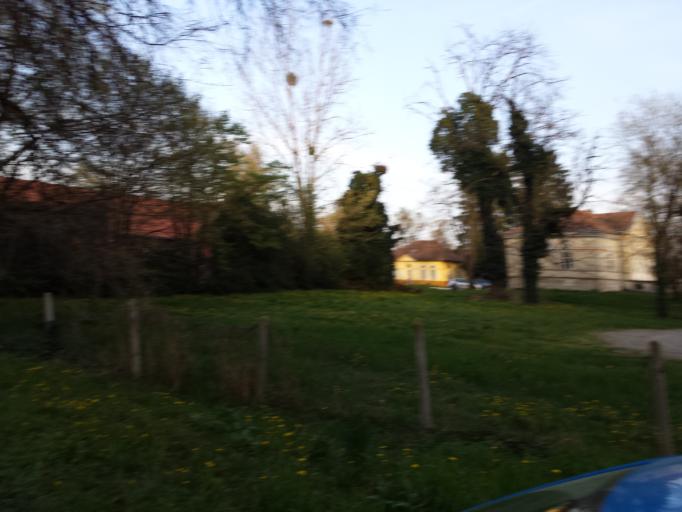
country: HR
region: Grad Zagreb
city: Dubrava
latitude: 45.8252
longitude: 16.0266
